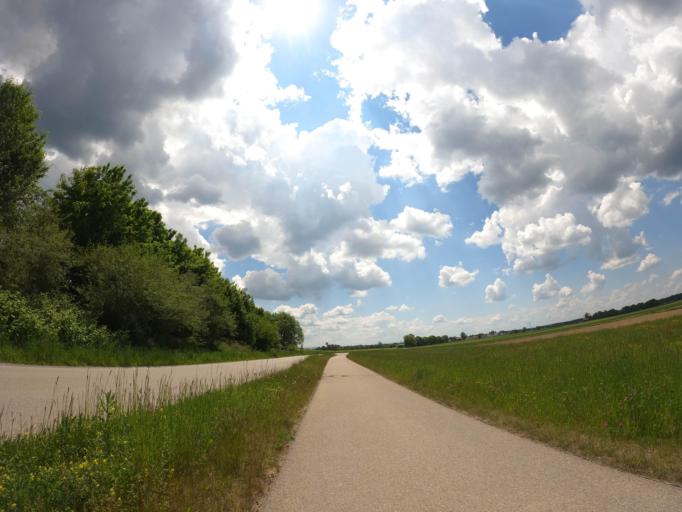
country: DE
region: Bavaria
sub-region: Upper Bavaria
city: Sauerlach
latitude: 47.9872
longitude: 11.6588
